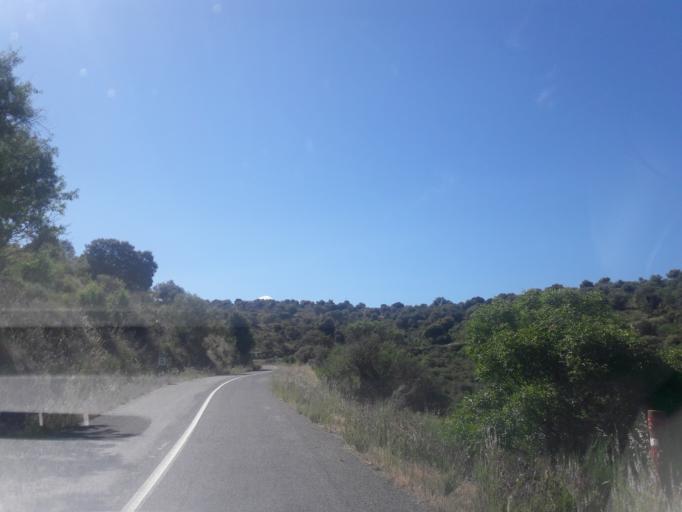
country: ES
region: Castille and Leon
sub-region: Provincia de Salamanca
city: Saucelle
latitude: 41.0130
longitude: -6.7425
